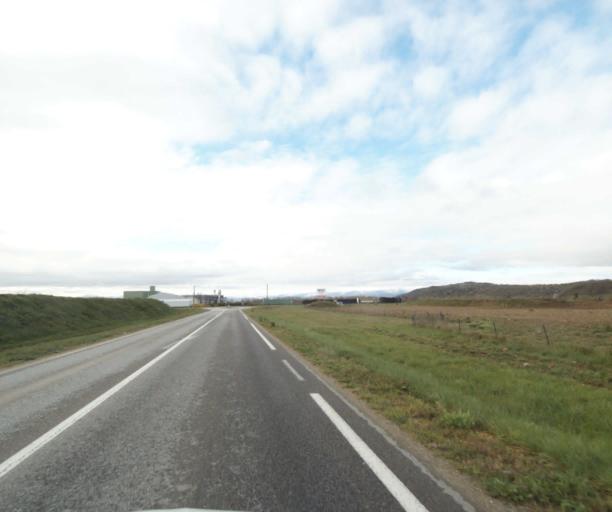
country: FR
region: Midi-Pyrenees
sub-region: Departement de l'Ariege
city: Saverdun
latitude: 43.2054
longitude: 1.6088
